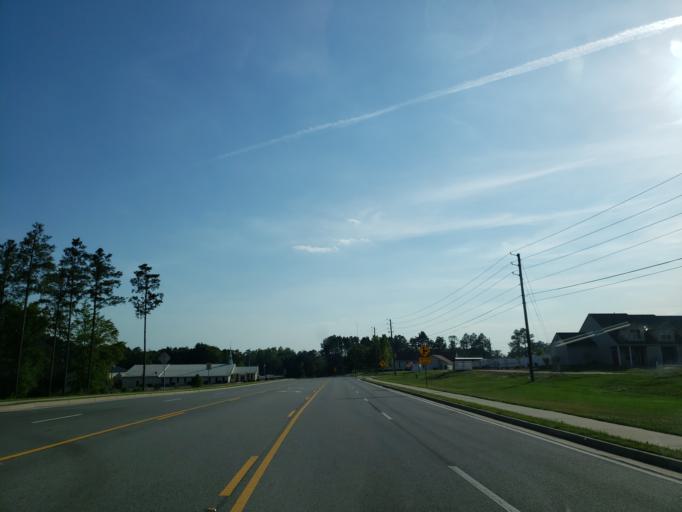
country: US
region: Georgia
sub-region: Tift County
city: Tifton
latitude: 31.4725
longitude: -83.5440
